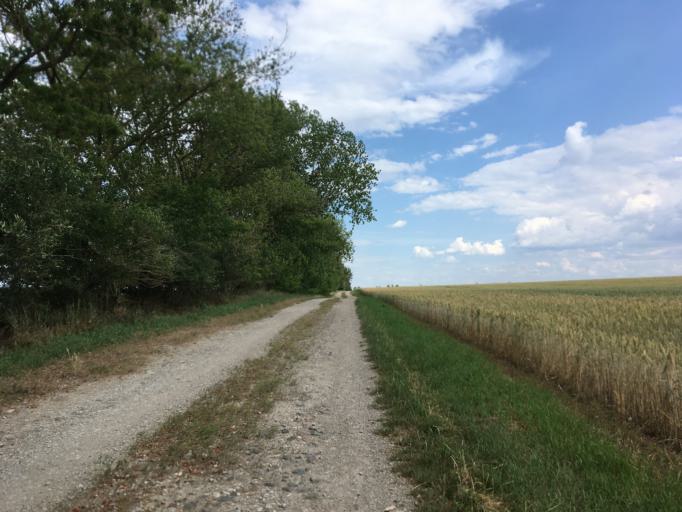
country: DE
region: Saxony-Anhalt
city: Baalberge
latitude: 51.7616
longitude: 11.8773
